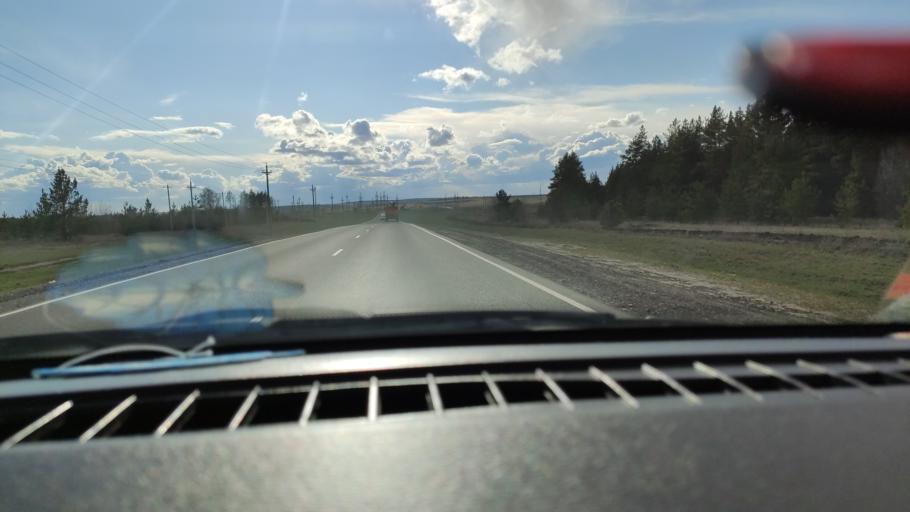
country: RU
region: Saratov
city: Sennoy
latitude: 52.1418
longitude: 46.9151
